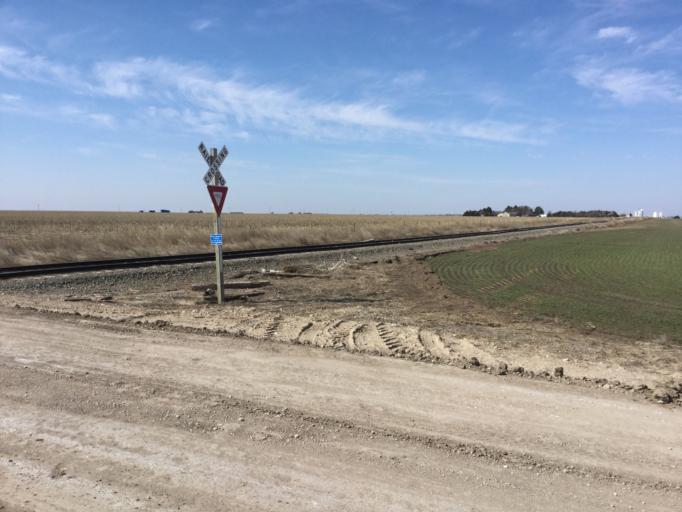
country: US
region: Kansas
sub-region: Scott County
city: Scott City
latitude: 38.4872
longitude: -100.8517
